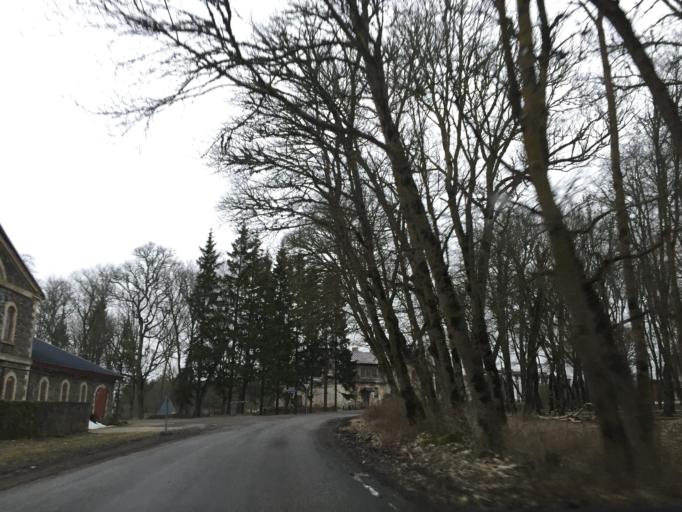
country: EE
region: Laeaene
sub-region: Lihula vald
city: Lihula
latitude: 58.6507
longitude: 23.6165
